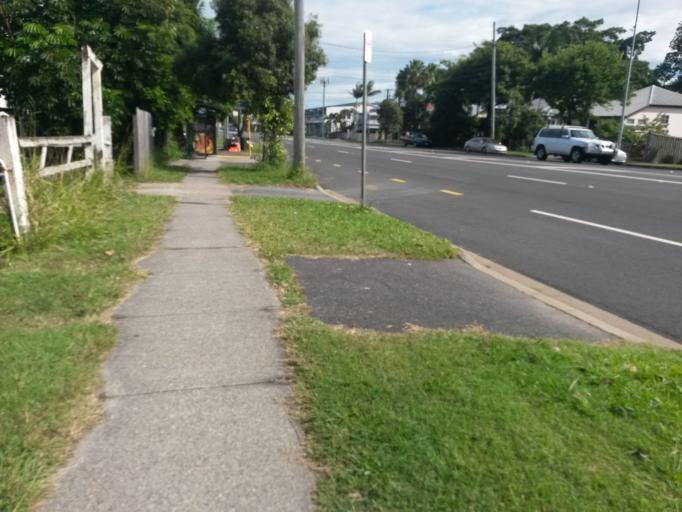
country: AU
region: Queensland
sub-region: Brisbane
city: Greenslopes
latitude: -27.4990
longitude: 153.0485
